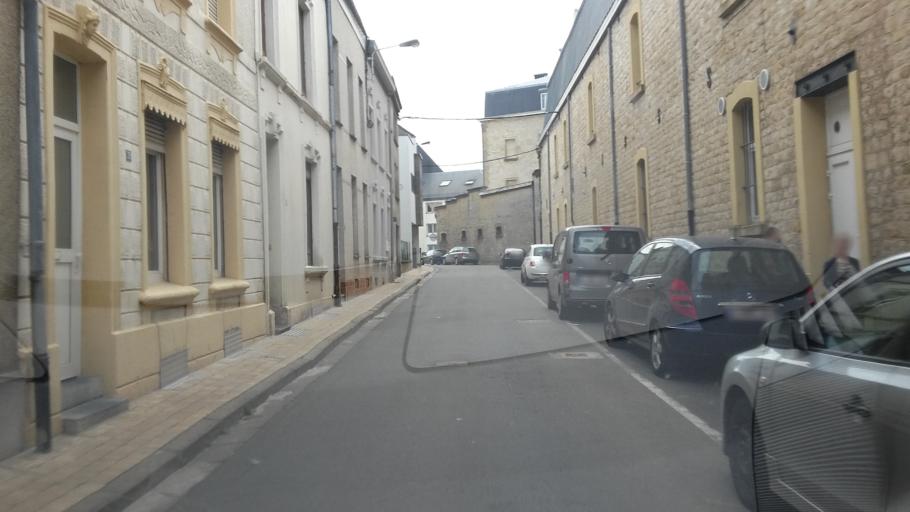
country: BE
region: Wallonia
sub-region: Province du Luxembourg
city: Arlon
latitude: 49.6856
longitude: 5.8178
